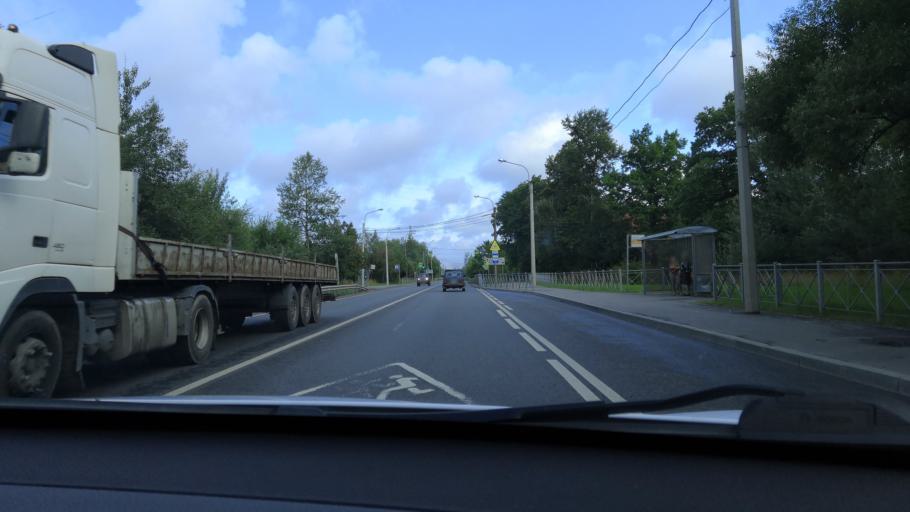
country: RU
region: St.-Petersburg
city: Tyarlevo
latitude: 59.7007
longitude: 30.4407
